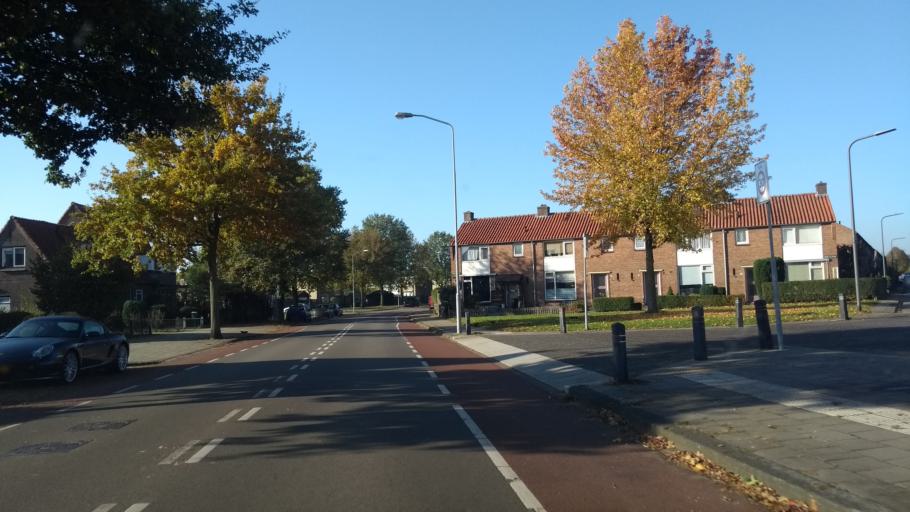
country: NL
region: Gelderland
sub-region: Gemeente Rheden
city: Rheden
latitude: 52.0019
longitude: 6.0300
